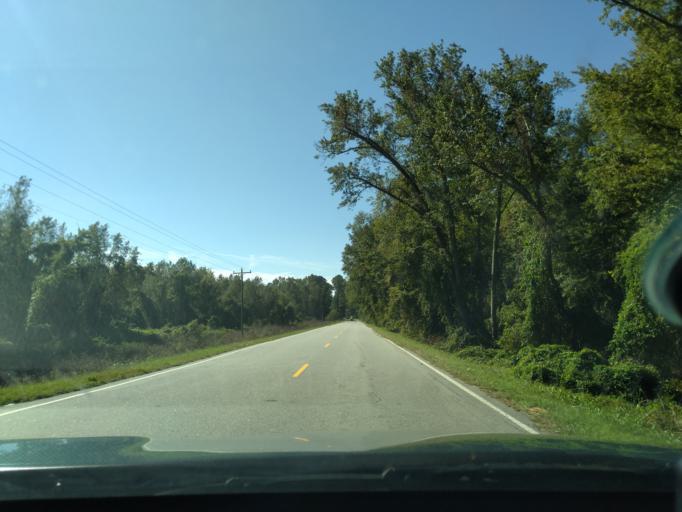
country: US
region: North Carolina
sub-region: Washington County
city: Plymouth
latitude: 35.7331
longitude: -76.7445
